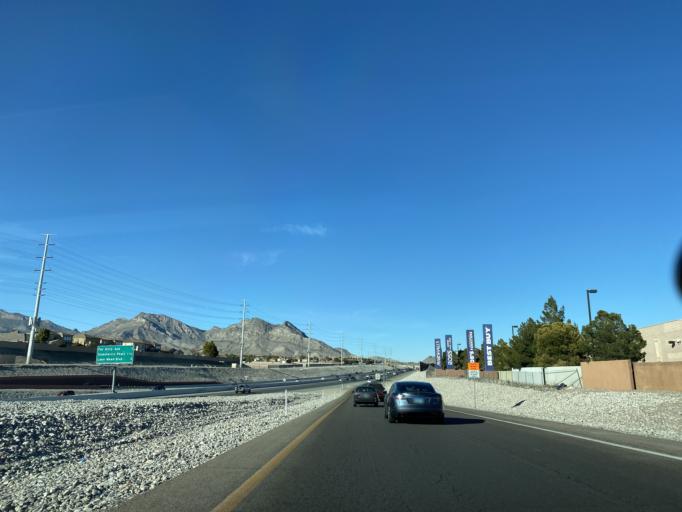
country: US
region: Nevada
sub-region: Clark County
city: Summerlin South
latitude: 36.1612
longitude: -115.3367
